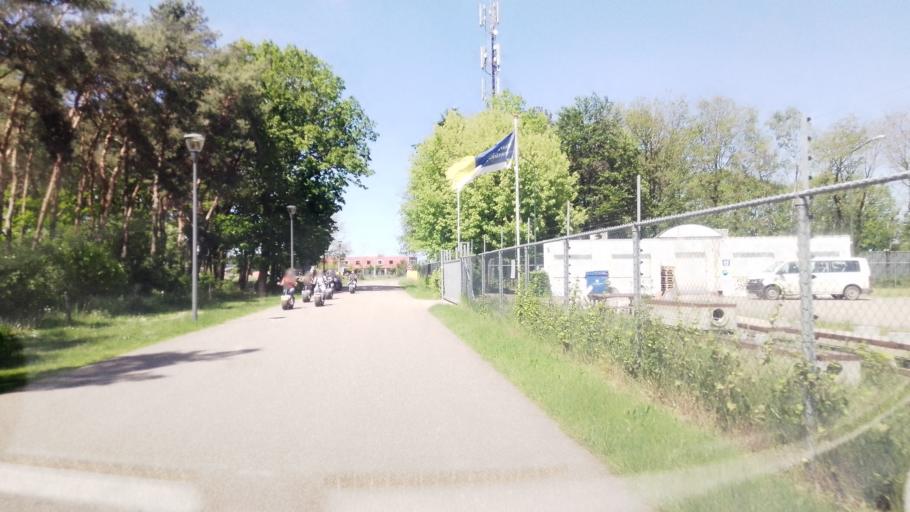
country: NL
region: Limburg
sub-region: Gemeente Venlo
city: Venlo
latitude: 51.4079
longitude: 6.1137
